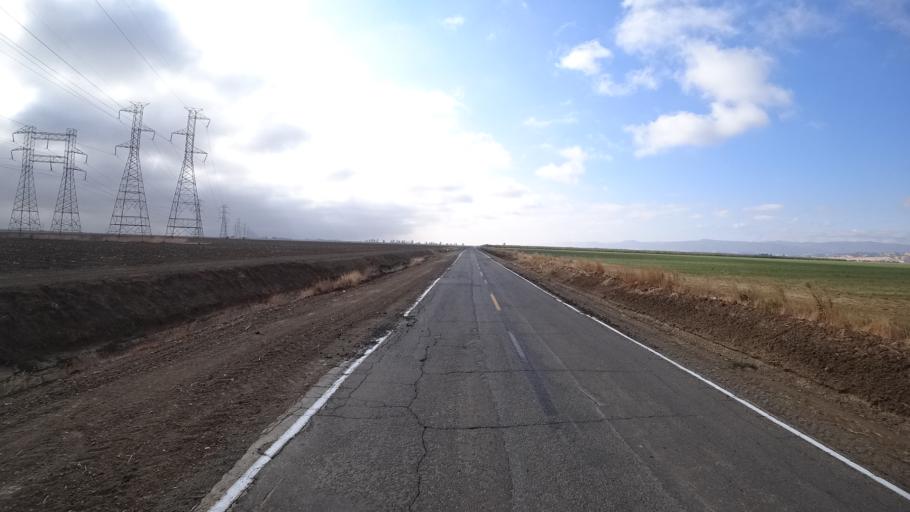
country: US
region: California
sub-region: Yolo County
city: Esparto
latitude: 38.7680
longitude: -122.0071
